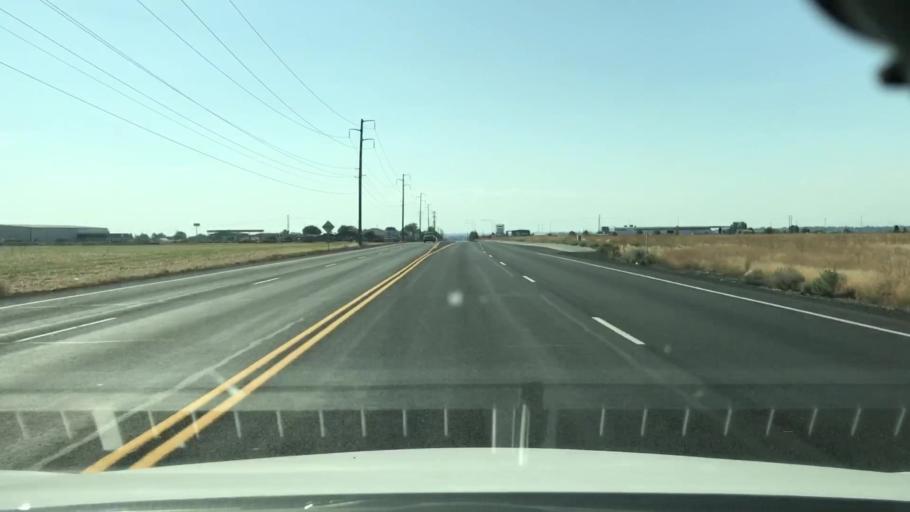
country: US
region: Washington
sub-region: Grant County
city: Moses Lake
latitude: 47.1310
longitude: -119.2429
